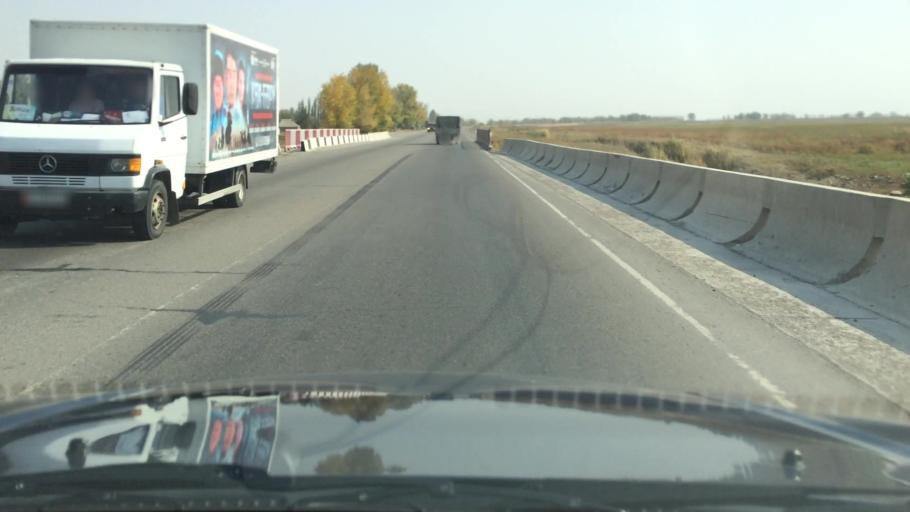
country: KG
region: Chuy
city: Lebedinovka
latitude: 42.9210
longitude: 74.7376
